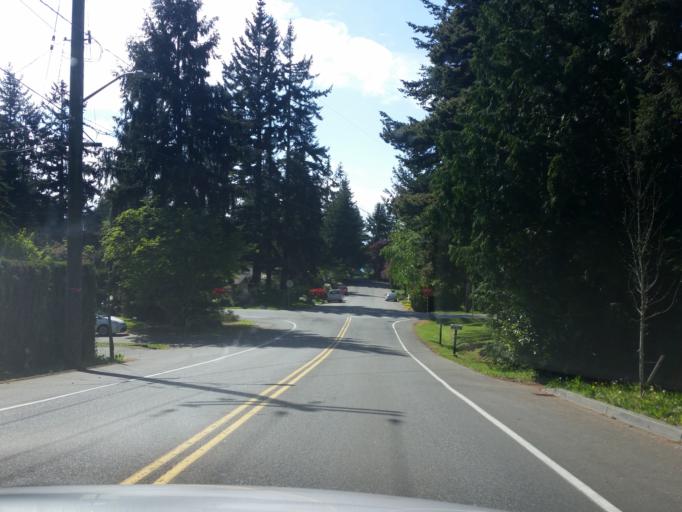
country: US
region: Washington
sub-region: Snohomish County
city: Esperance
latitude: 47.7742
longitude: -122.3604
